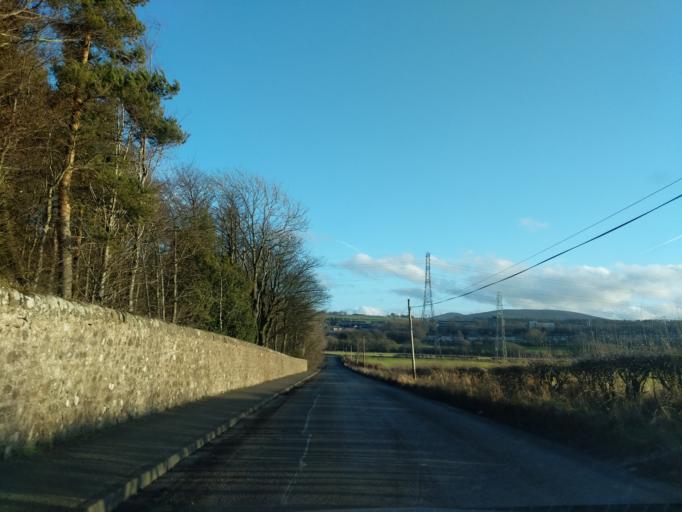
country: GB
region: Scotland
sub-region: Edinburgh
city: Currie
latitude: 55.9033
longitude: -3.3240
